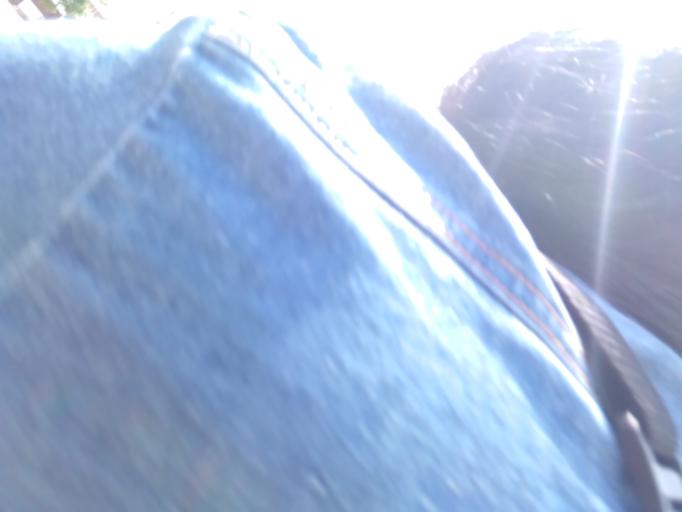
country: CO
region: Antioquia
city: San Carlos
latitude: 7.8856
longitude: -74.8086
